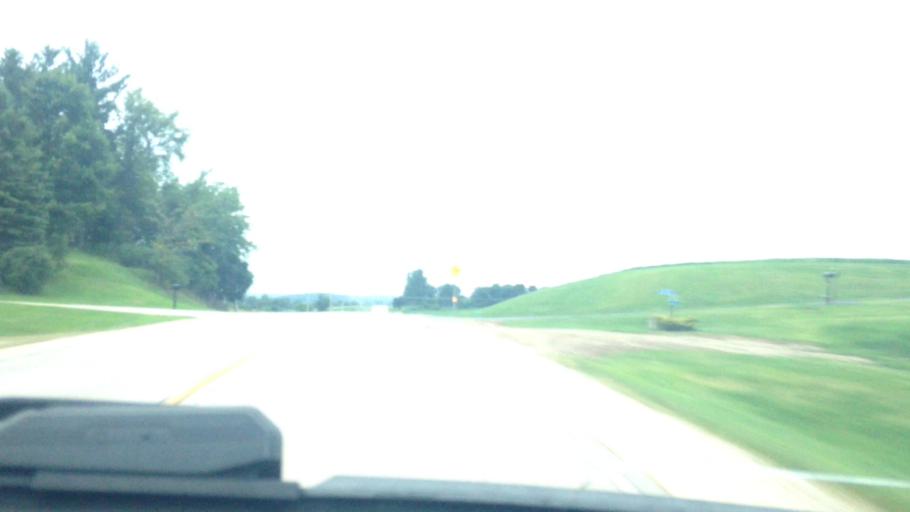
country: US
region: Wisconsin
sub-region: Dodge County
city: Mayville
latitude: 43.4512
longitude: -88.4962
